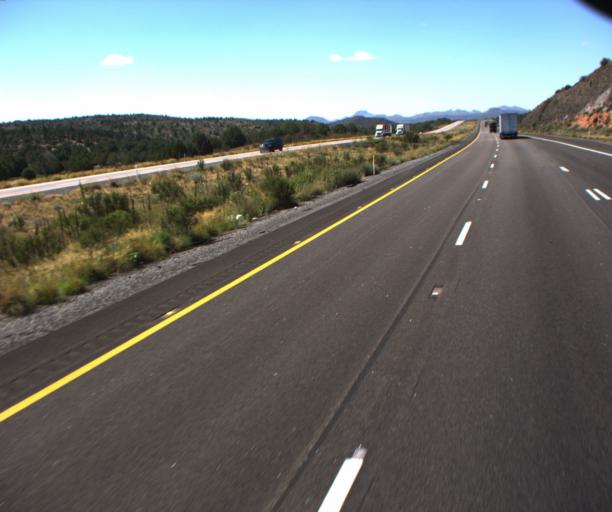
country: US
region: Arizona
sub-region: Mohave County
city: Peach Springs
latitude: 35.2019
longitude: -113.3023
